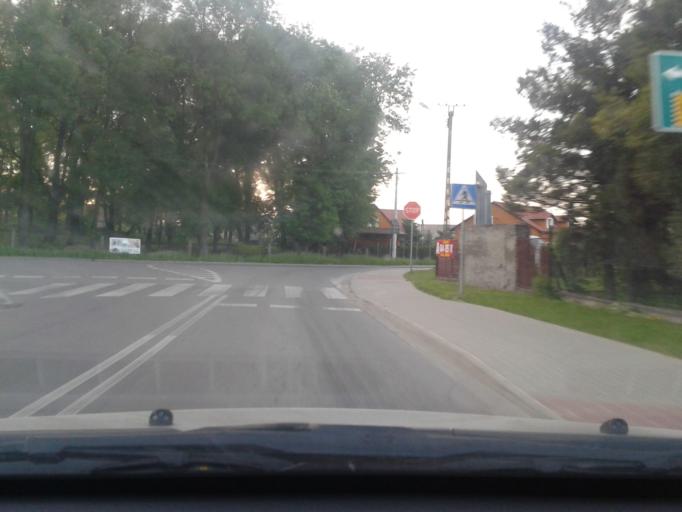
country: PL
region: Lesser Poland Voivodeship
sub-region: Powiat oswiecimski
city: Rajsko
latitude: 50.0077
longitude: 19.1907
